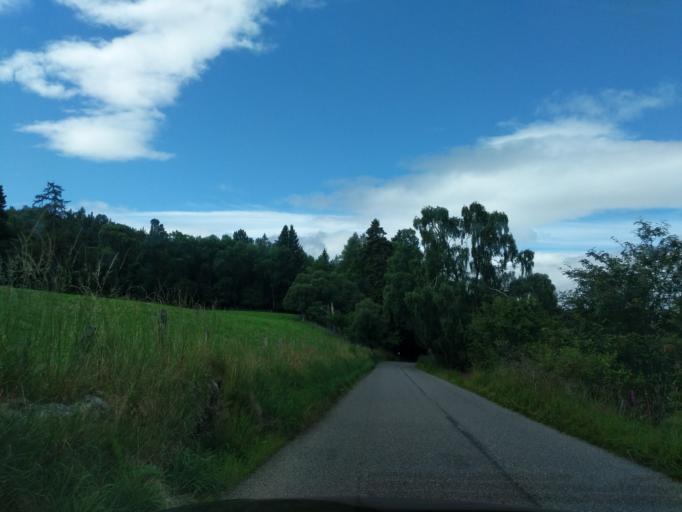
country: GB
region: Scotland
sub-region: Aberdeenshire
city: Ballater
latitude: 57.0384
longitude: -3.1874
